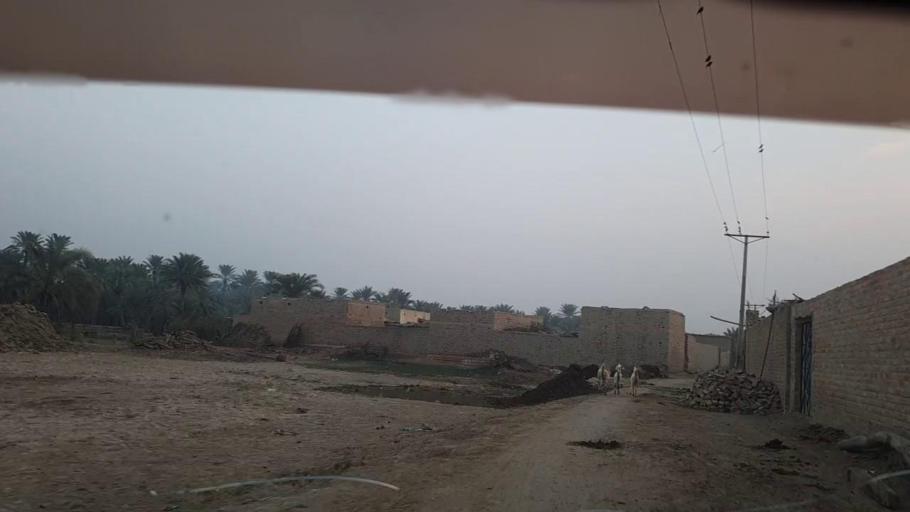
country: PK
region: Sindh
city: Khairpur
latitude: 27.5806
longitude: 68.7385
